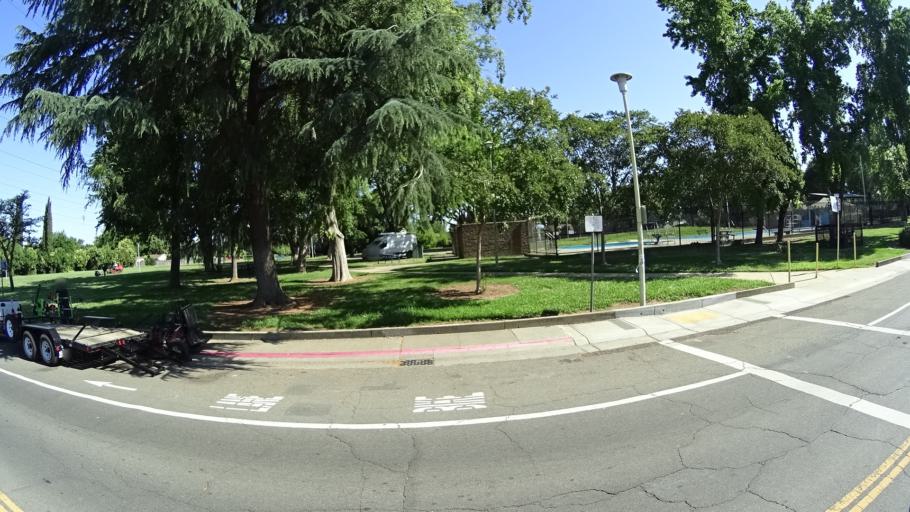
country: US
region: California
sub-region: Sacramento County
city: Rosemont
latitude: 38.5542
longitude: -121.3902
